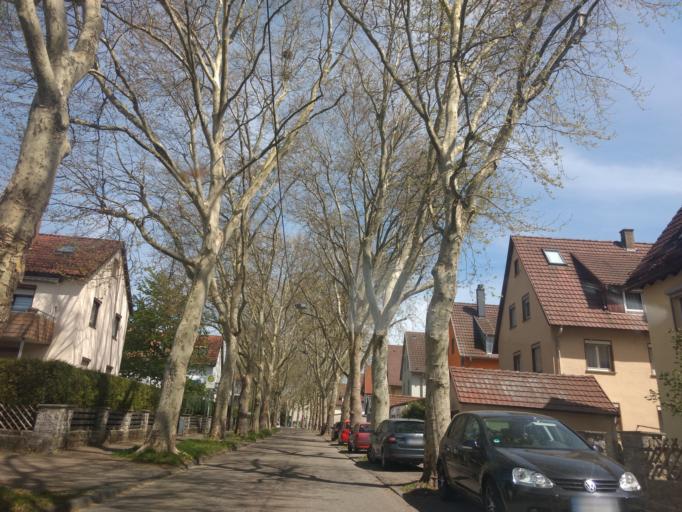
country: DE
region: Baden-Wuerttemberg
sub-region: Regierungsbezirk Stuttgart
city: Schwabisch Gmund
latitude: 48.7935
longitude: 9.7812
